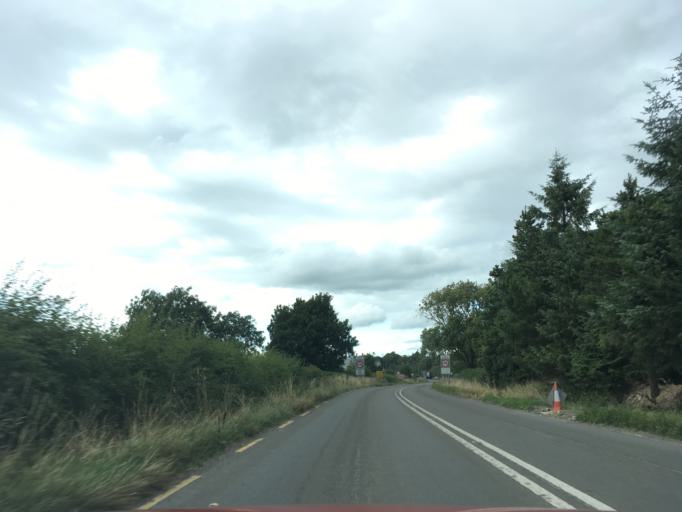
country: IE
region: Munster
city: Cahir
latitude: 52.4316
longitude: -7.8860
